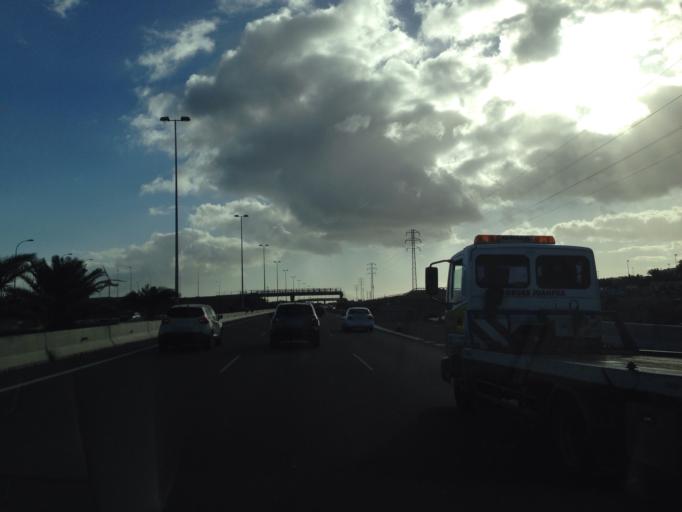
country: ES
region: Canary Islands
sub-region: Provincia de Las Palmas
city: Cruce de Arinaga
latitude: 27.8555
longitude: -15.4292
